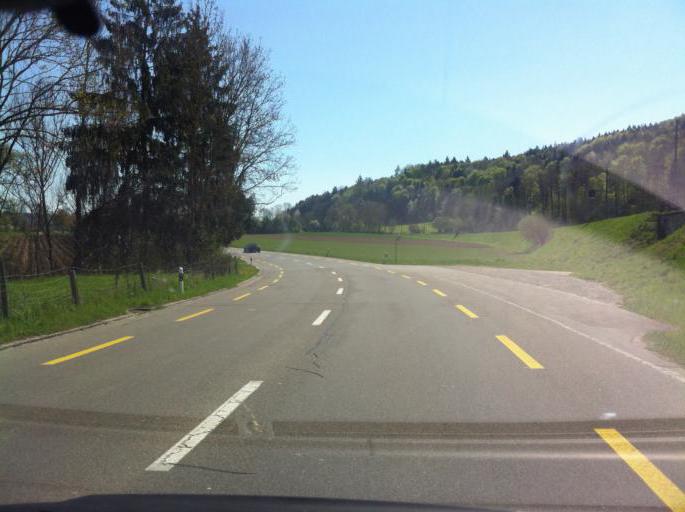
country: DE
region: Baden-Wuerttemberg
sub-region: Freiburg Region
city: Busingen
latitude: 47.6828
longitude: 8.6713
